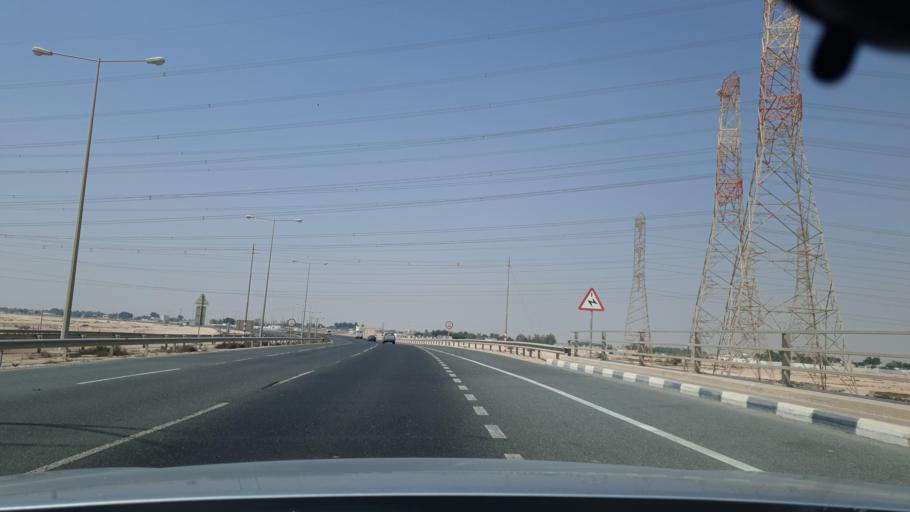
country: QA
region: Al Khawr
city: Al Khawr
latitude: 25.7555
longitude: 51.4740
